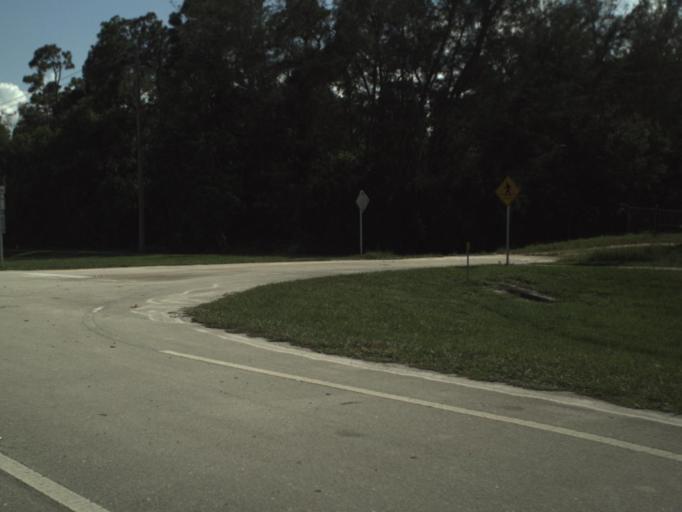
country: US
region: Florida
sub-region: Palm Beach County
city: Wellington
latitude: 26.5875
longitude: -80.2061
